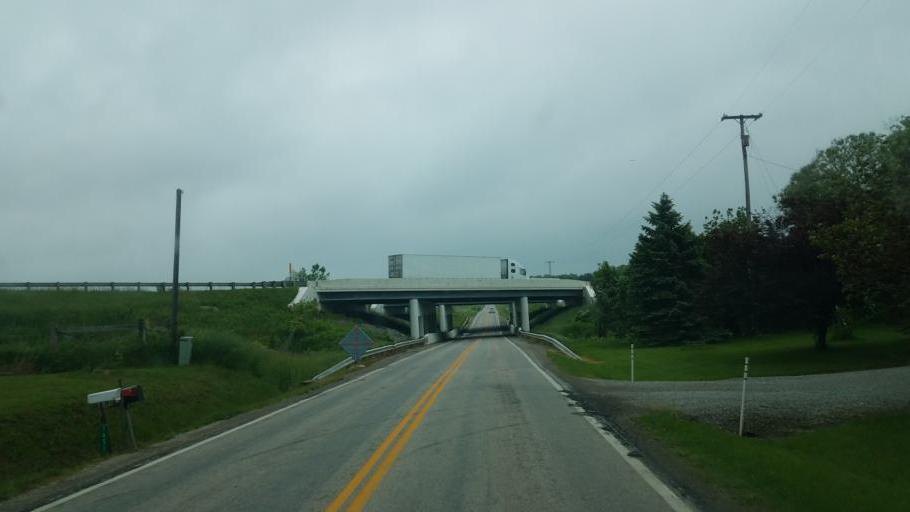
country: US
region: Ohio
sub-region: Ashland County
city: Ashland
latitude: 40.8218
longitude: -82.3357
